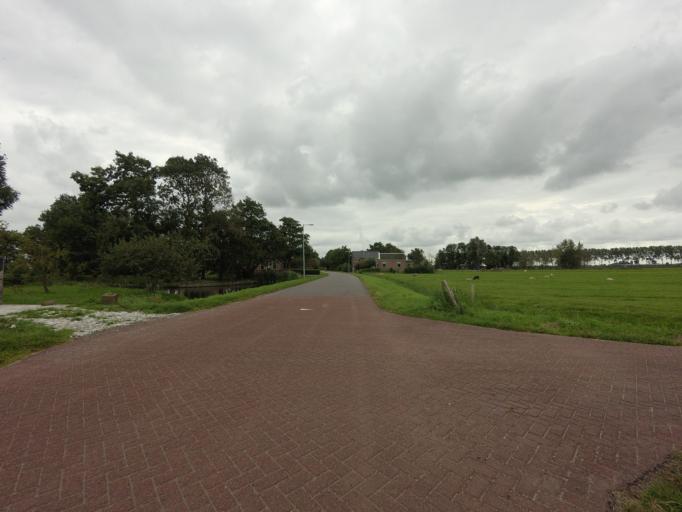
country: NL
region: North Holland
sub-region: Gemeente Edam-Volendam
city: Edam
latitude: 52.5424
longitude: 5.0114
